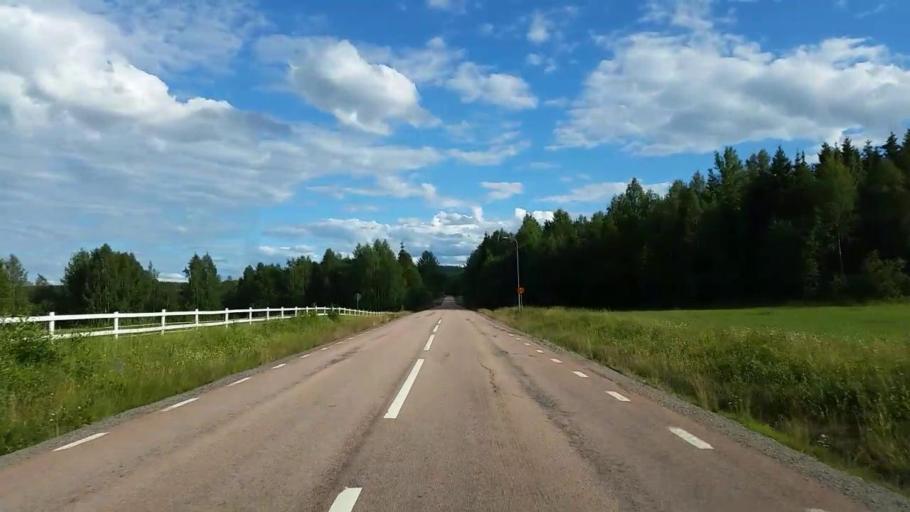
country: SE
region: Gaevleborg
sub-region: Ljusdals Kommun
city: Farila
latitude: 61.9053
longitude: 15.8943
